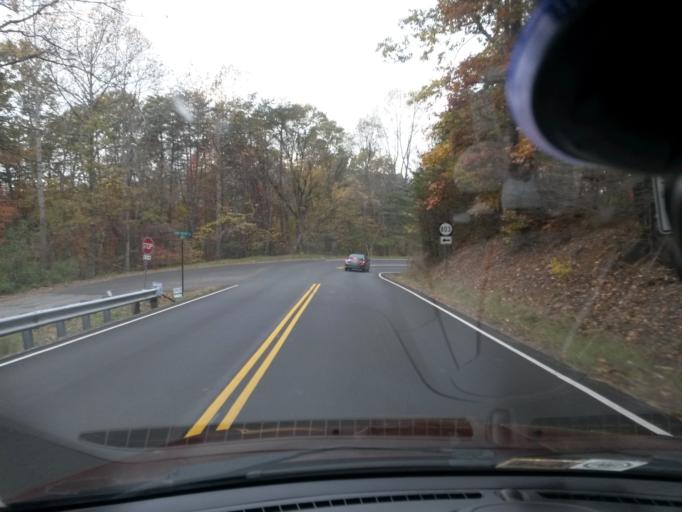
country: US
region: Virginia
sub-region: Roanoke County
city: Vinton
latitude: 37.2123
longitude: -79.8871
